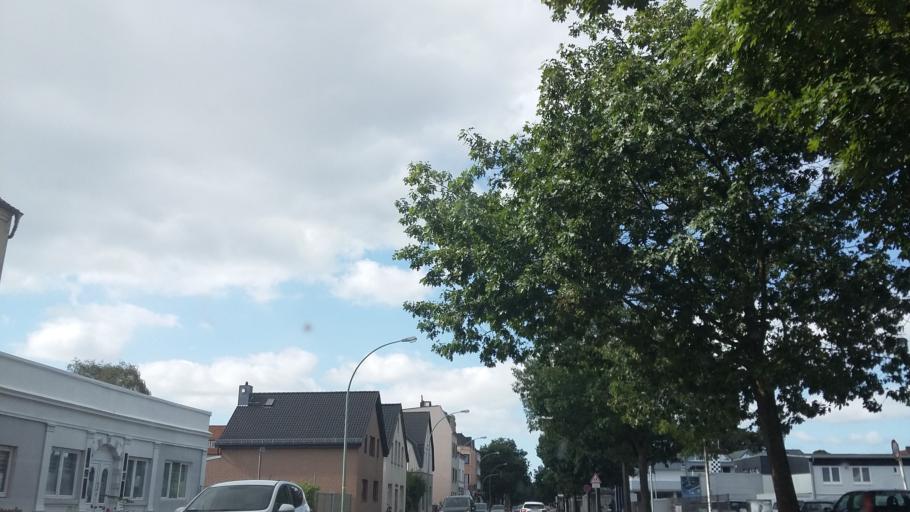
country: DE
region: Bremen
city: Bremerhaven
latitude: 53.5143
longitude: 8.5935
